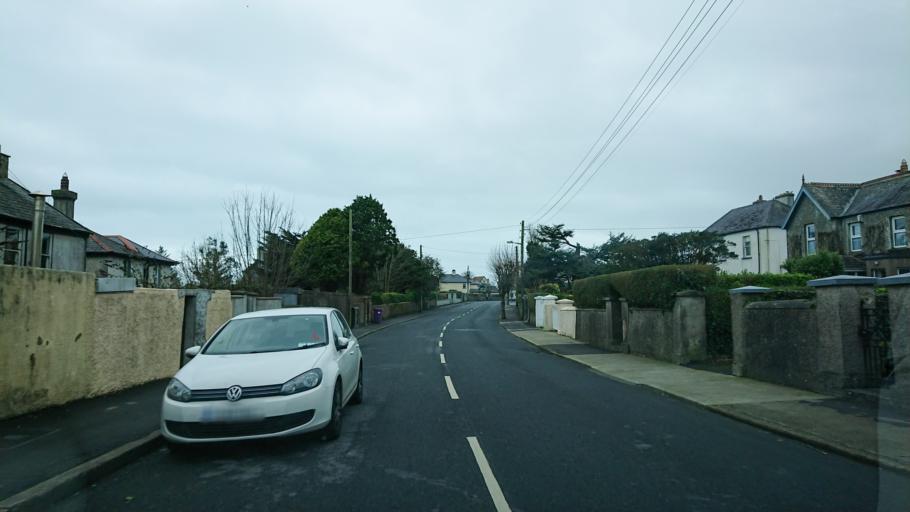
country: IE
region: Munster
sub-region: Waterford
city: Tra Mhor
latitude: 52.1605
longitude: -7.1563
